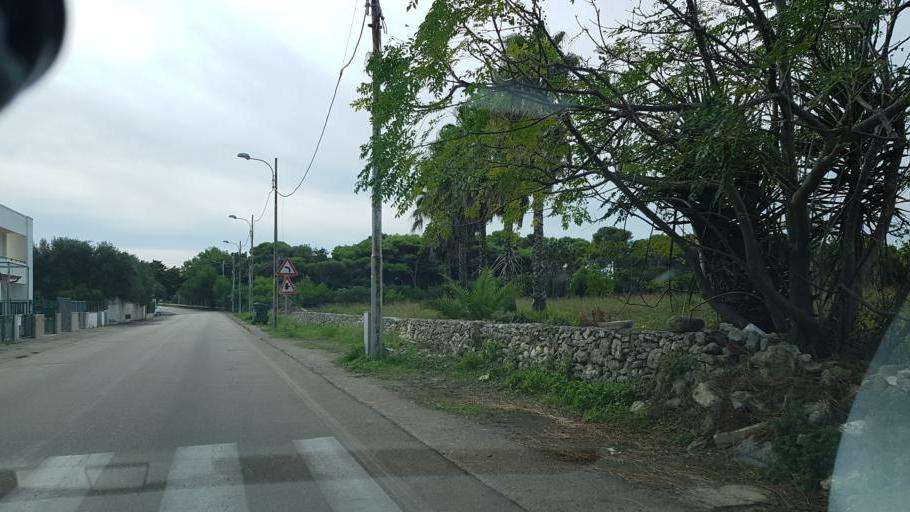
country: IT
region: Apulia
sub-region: Provincia di Lecce
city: Borgagne
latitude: 40.2905
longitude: 18.4232
